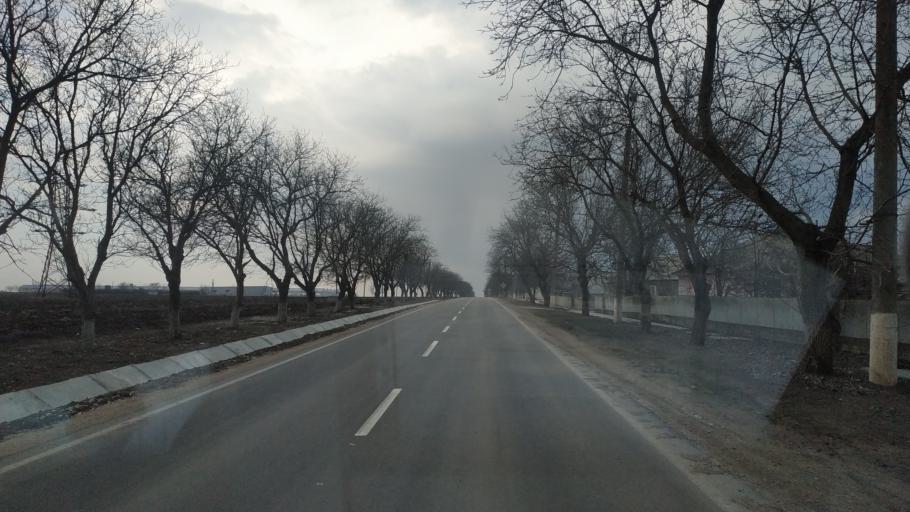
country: MD
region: Telenesti
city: Grigoriopol
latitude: 47.0133
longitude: 29.2889
